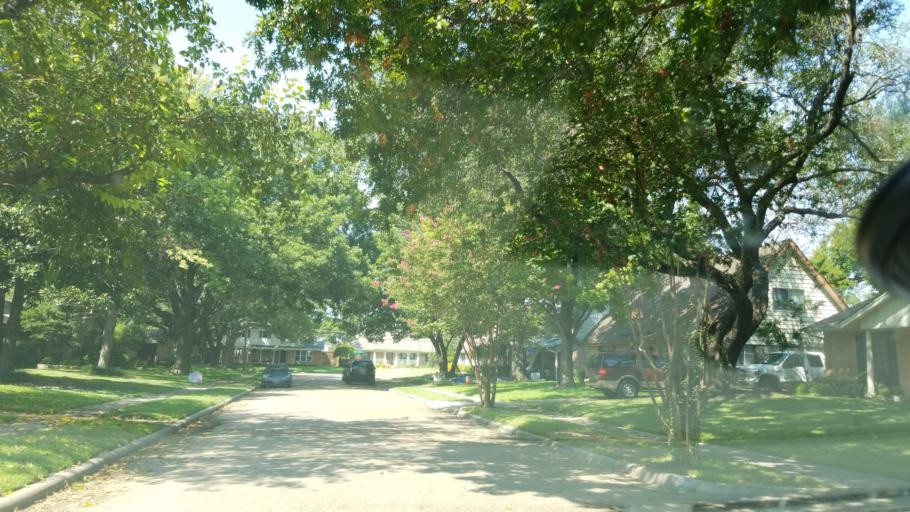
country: US
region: Texas
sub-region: Dallas County
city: Richardson
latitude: 32.8784
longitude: -96.7138
